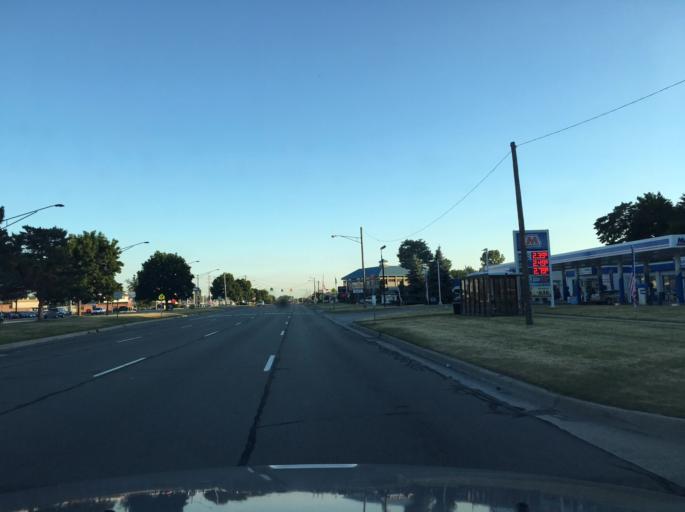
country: US
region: Michigan
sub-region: Macomb County
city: Clinton
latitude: 42.5648
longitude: -82.8945
